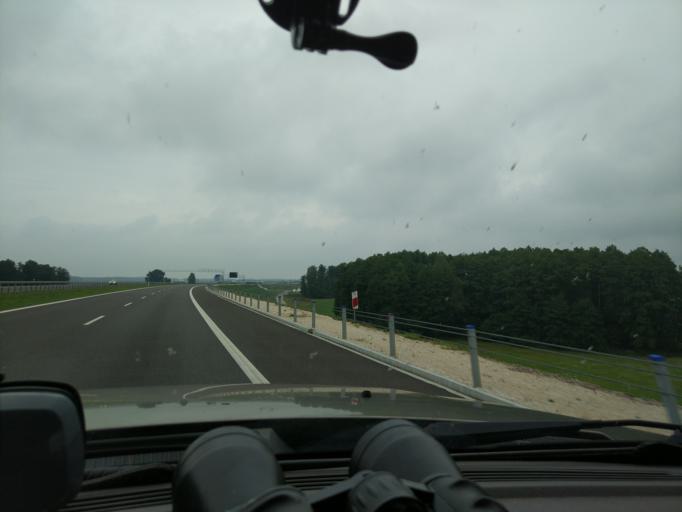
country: PL
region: Podlasie
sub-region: Powiat zambrowski
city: Szumowo
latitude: 52.9436
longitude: 22.1529
